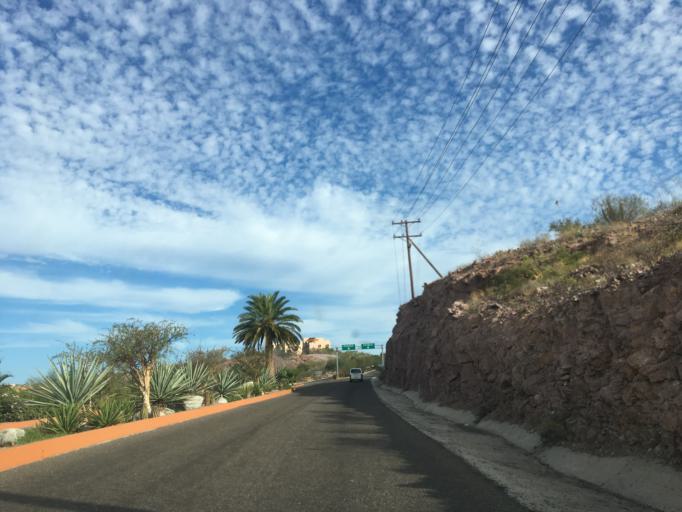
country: MX
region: Baja California Sur
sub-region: La Paz
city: La Paz
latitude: 24.2071
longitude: -110.2983
